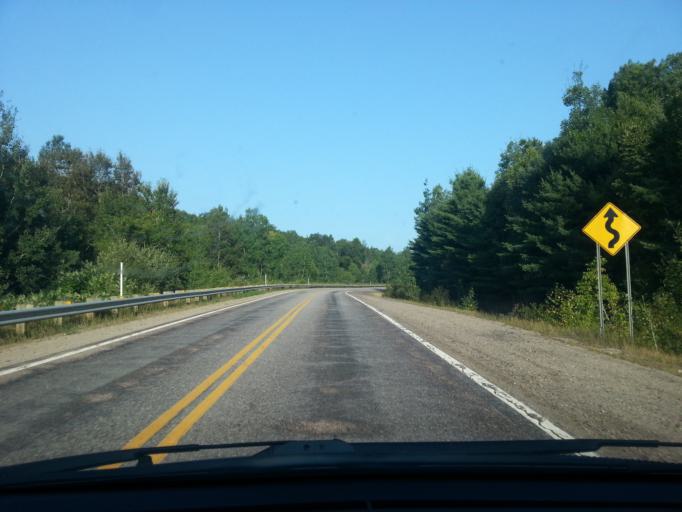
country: CA
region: Quebec
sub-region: Outaouais
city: Maniwaki
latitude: 46.1051
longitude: -76.1140
